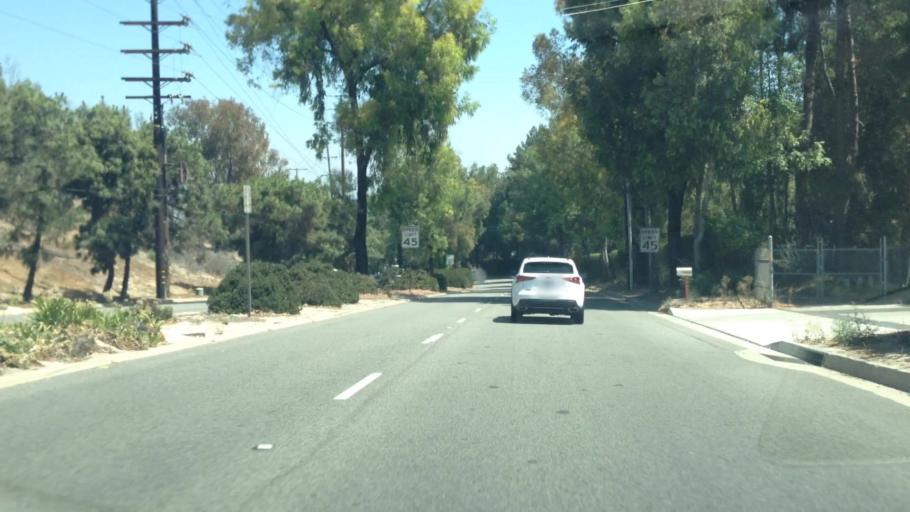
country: US
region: California
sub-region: Los Angeles County
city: Rolling Hills Estates
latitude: 33.7923
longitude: -118.3512
